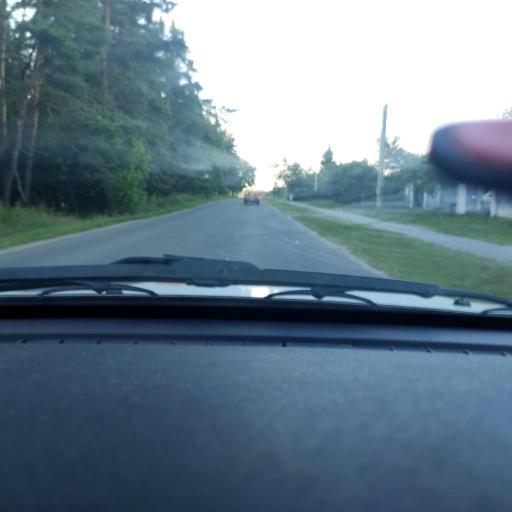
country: RU
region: Voronezj
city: Ramon'
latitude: 51.8982
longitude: 39.2858
